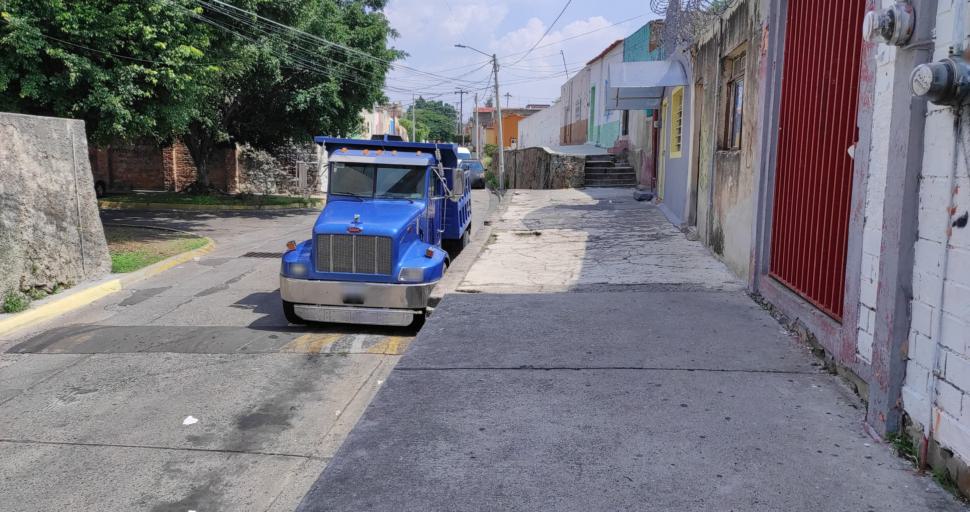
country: MX
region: Jalisco
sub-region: Zapopan
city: Zapopan
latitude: 20.7120
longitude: -103.3547
